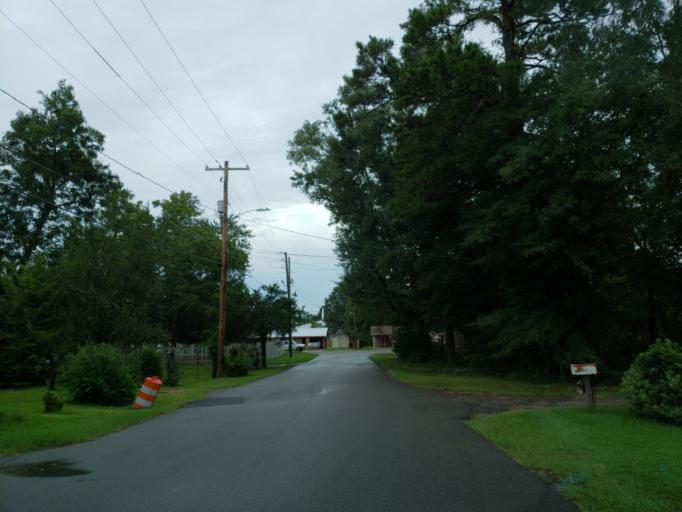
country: US
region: Mississippi
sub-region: Forrest County
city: Hattiesburg
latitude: 31.3094
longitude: -89.2941
